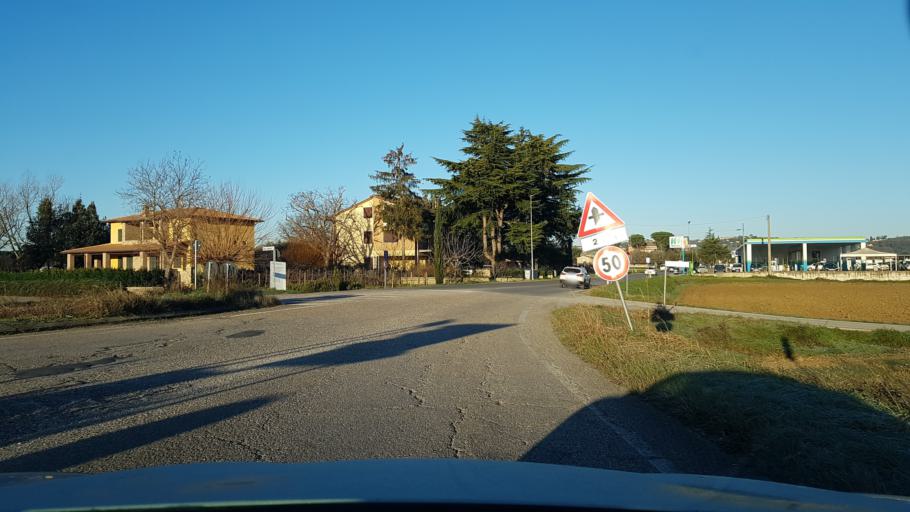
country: IT
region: Umbria
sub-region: Provincia di Perugia
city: San Martino in Campo
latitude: 43.0366
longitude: 12.4161
